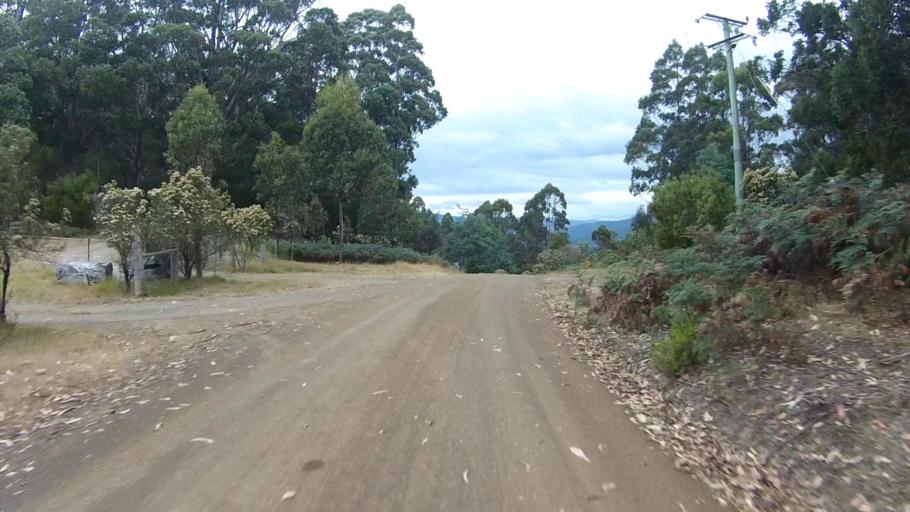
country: AU
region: Tasmania
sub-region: Huon Valley
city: Huonville
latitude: -42.9533
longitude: 147.0463
